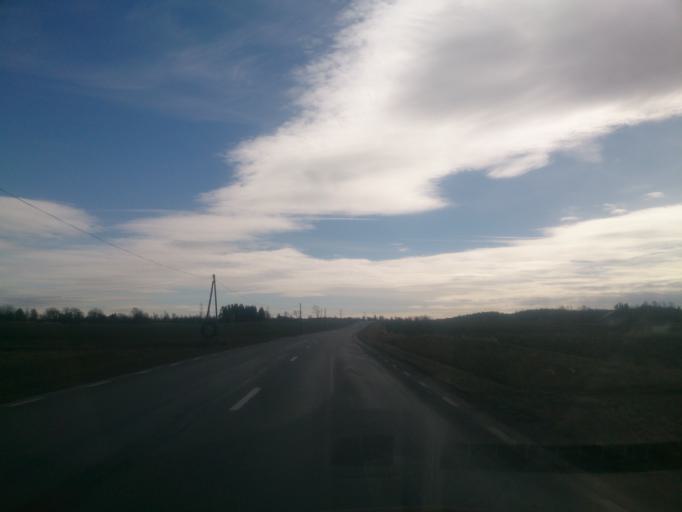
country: SE
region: OEstergoetland
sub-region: Norrkopings Kommun
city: Skarblacka
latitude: 58.6041
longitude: 15.8249
